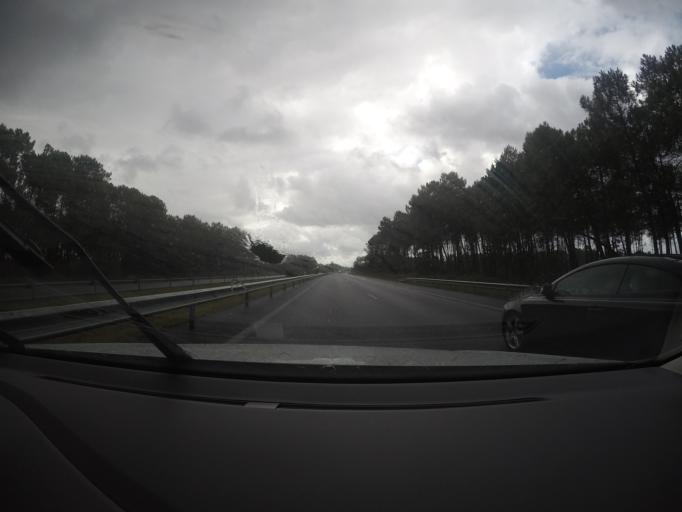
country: FR
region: Aquitaine
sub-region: Departement de la Gironde
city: Salles
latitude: 44.5600
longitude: -0.8321
